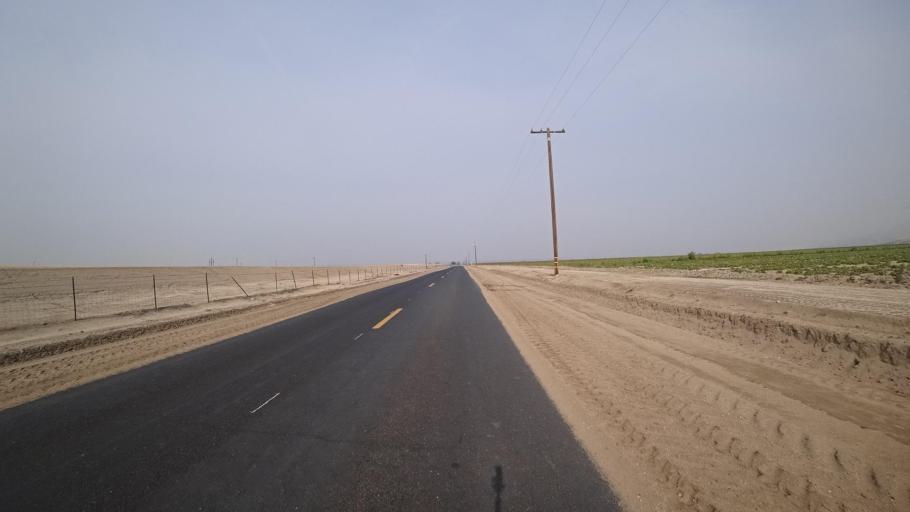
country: US
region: California
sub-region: Kern County
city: Arvin
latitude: 35.1252
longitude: -118.8506
